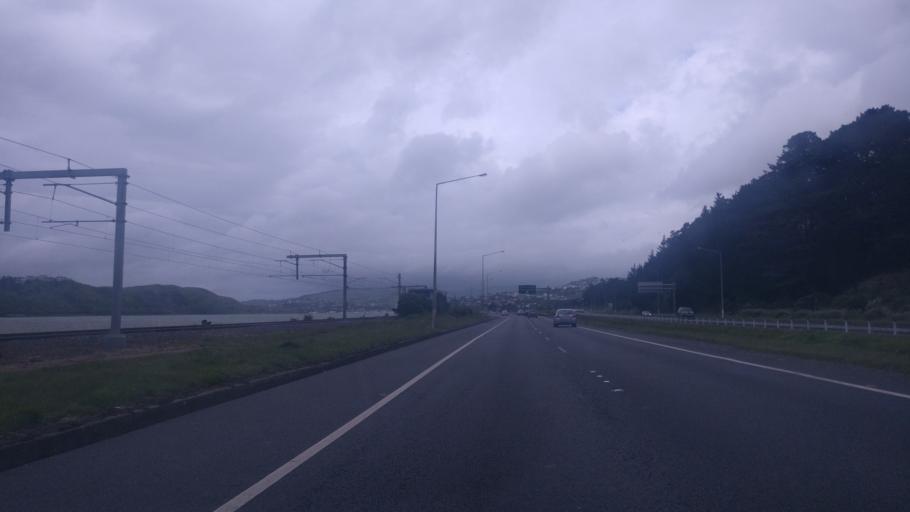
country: NZ
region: Wellington
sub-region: Porirua City
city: Porirua
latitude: -41.1245
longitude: 174.8491
